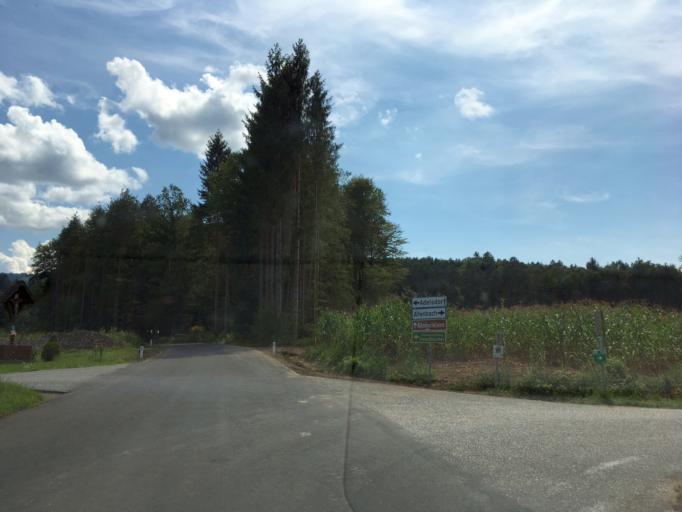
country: AT
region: Styria
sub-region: Politischer Bezirk Leibnitz
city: Oberhaag
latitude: 46.6805
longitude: 15.3515
